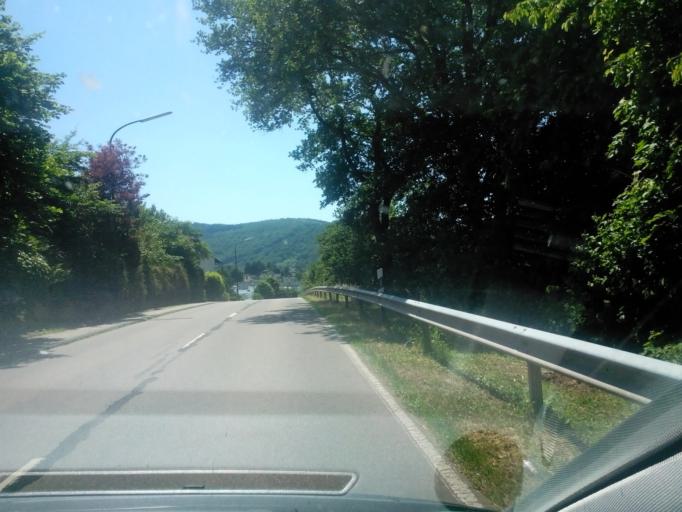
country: DE
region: Rheinland-Pfalz
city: Ockfen
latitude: 49.6120
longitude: 6.5635
